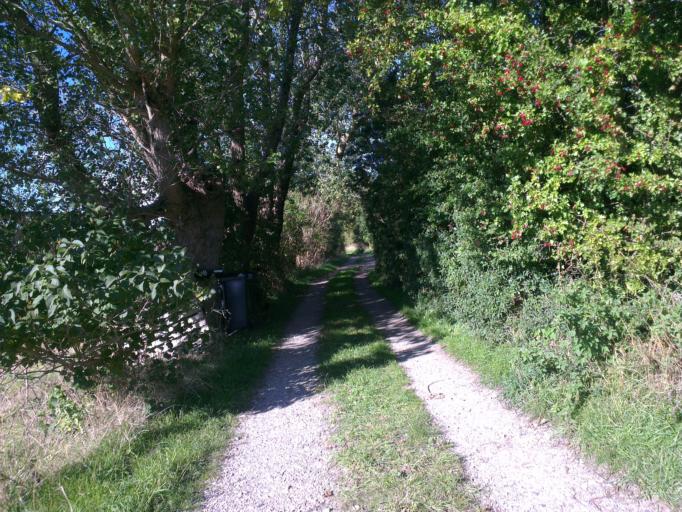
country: DK
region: Capital Region
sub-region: Frederikssund Kommune
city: Frederikssund
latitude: 55.7914
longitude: 12.0428
